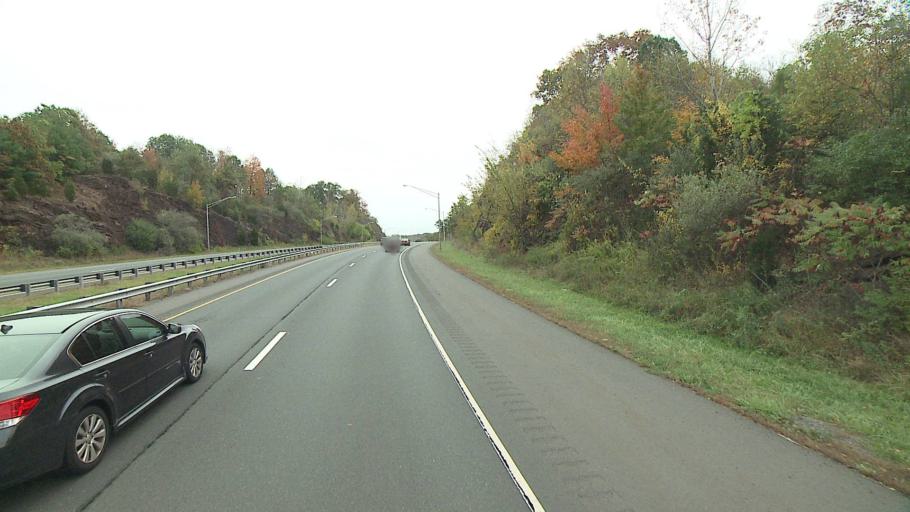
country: US
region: Connecticut
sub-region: Hartford County
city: Kensington
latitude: 41.6240
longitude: -72.7387
